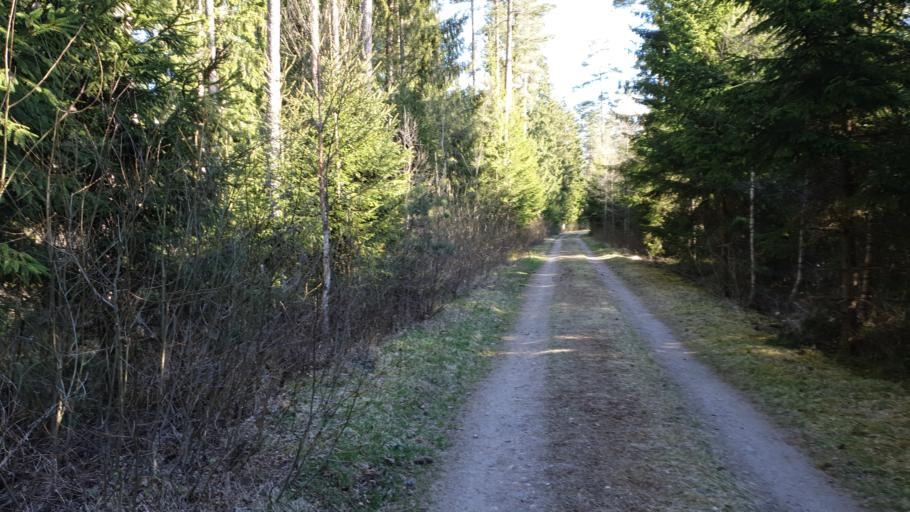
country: SE
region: Kronoberg
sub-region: Ljungby Kommun
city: Ljungby
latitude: 56.8312
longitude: 13.9021
